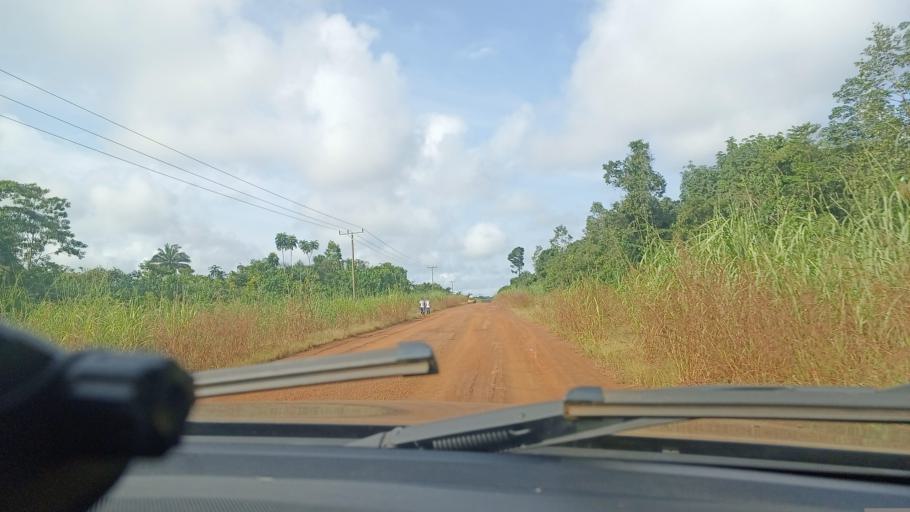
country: LR
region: Grand Cape Mount
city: Robertsport
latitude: 6.7015
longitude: -11.0923
